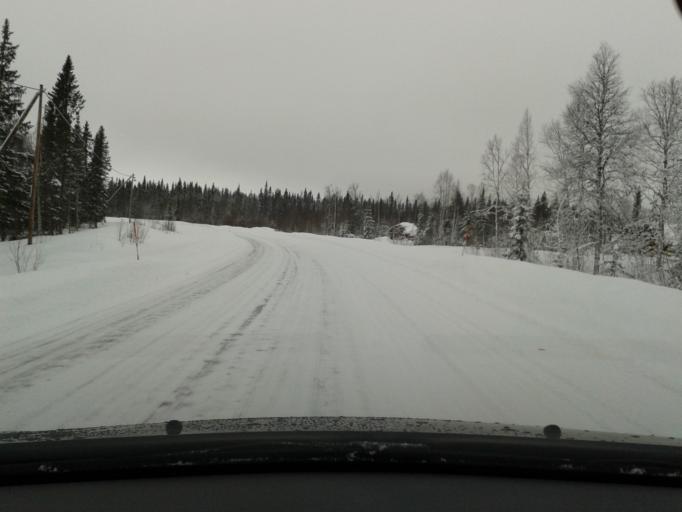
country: SE
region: Vaesterbotten
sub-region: Vilhelmina Kommun
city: Sjoberg
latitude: 65.1836
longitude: 15.8935
